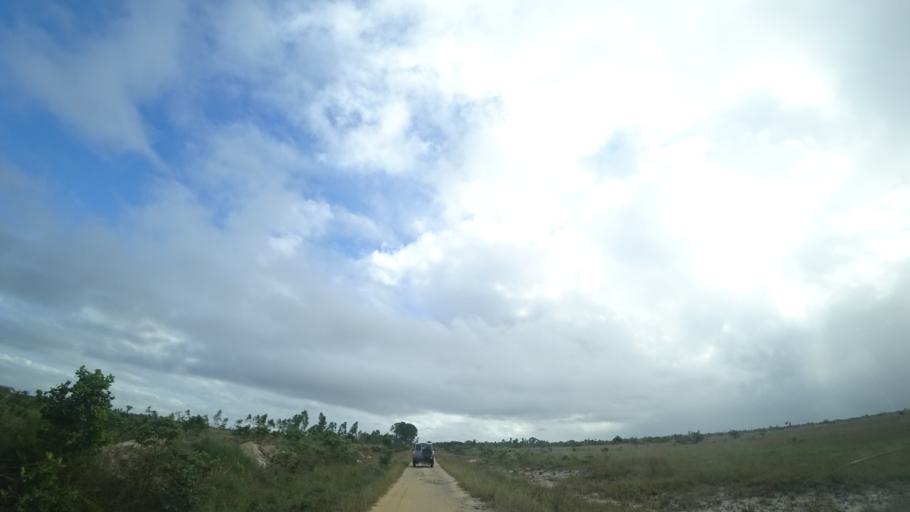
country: MZ
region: Sofala
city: Beira
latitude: -19.6254
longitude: 35.0604
